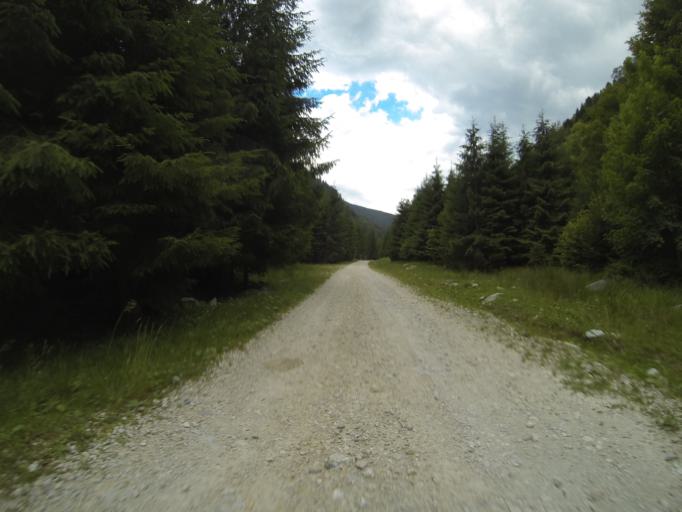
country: RO
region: Gorj
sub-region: Comuna Polovragi
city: Polovragi
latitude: 45.3175
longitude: 23.7953
